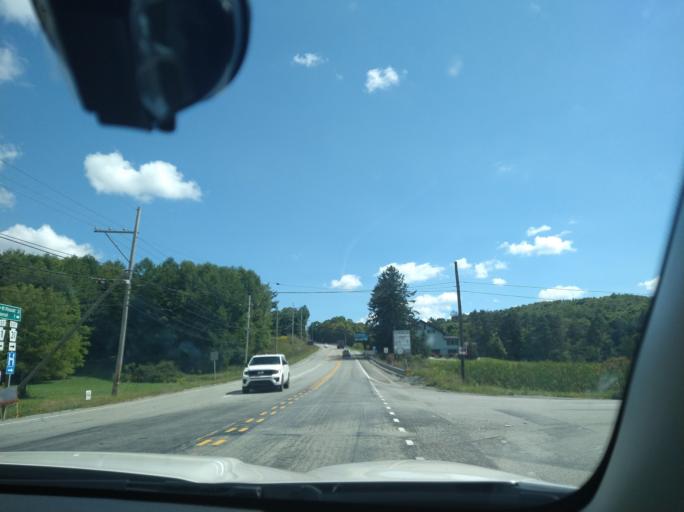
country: US
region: Pennsylvania
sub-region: Somerset County
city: Milford
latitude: 40.0311
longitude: -79.2093
